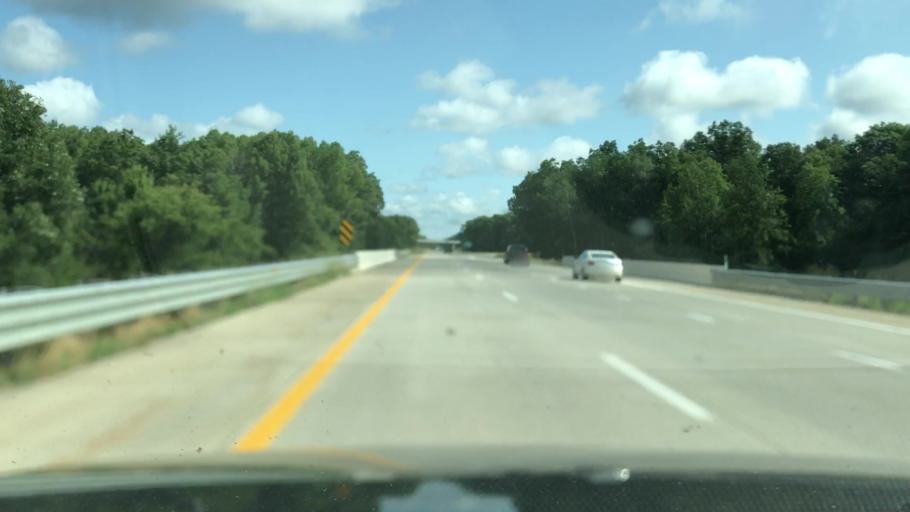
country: US
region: Michigan
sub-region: Montcalm County
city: Howard City
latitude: 43.3897
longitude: -85.5158
